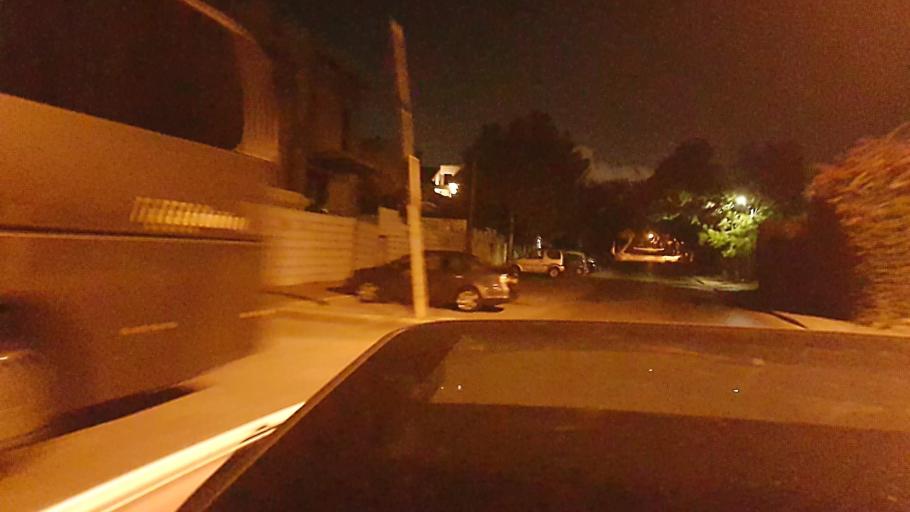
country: IL
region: Central District
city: Hod HaSharon
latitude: 32.1626
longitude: 34.8859
